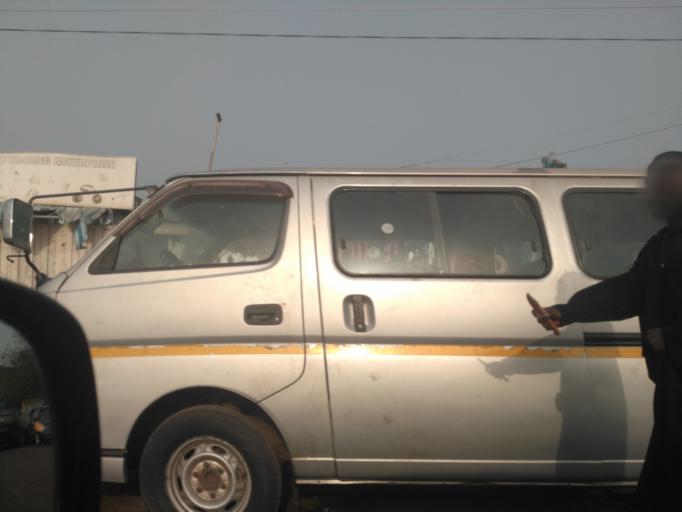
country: GH
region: Greater Accra
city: Accra
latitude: 5.5952
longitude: -0.1940
